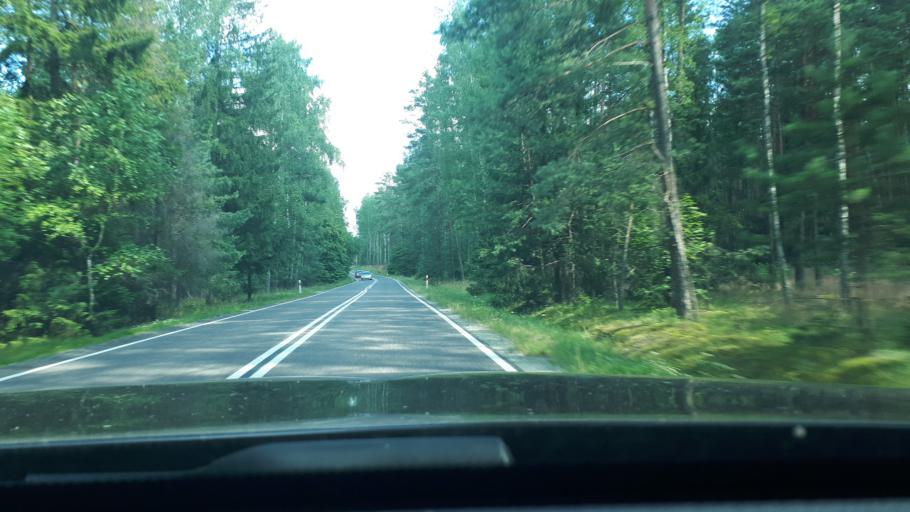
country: PL
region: Warmian-Masurian Voivodeship
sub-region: Powiat olsztynski
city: Stawiguda
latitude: 53.5354
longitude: 20.4302
